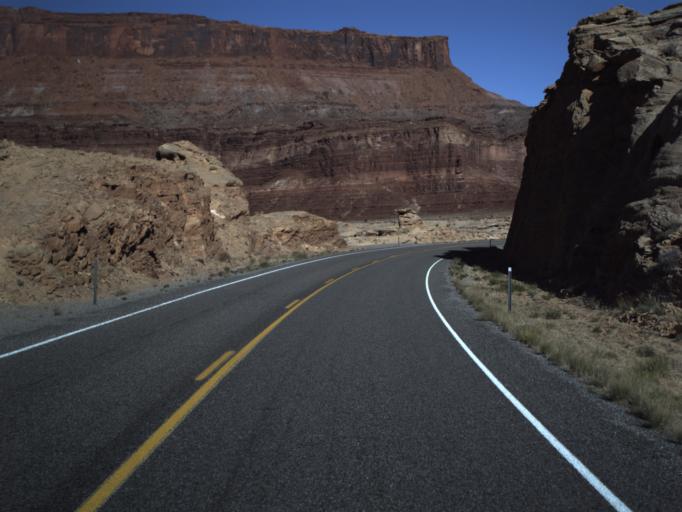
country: US
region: Utah
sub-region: San Juan County
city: Blanding
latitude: 37.9122
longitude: -110.3872
